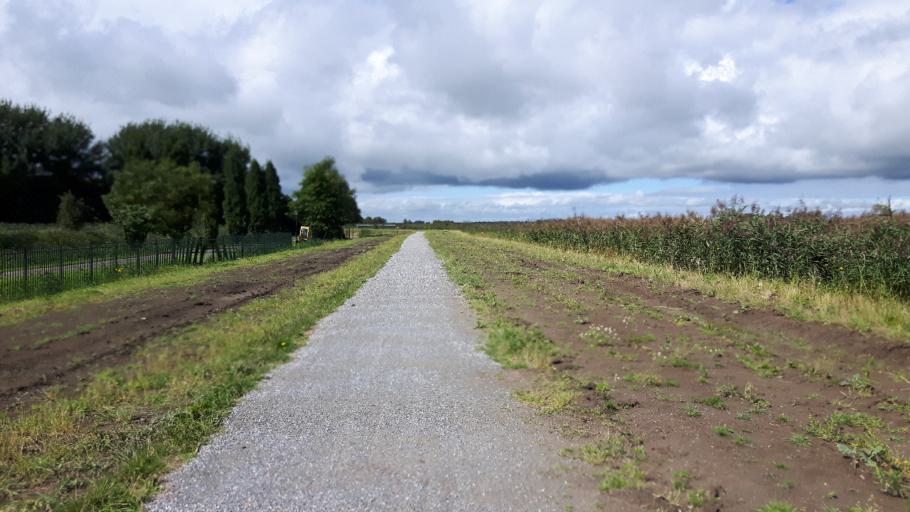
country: NL
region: Groningen
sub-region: Gemeente Slochteren
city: Slochteren
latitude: 53.2674
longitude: 6.8258
